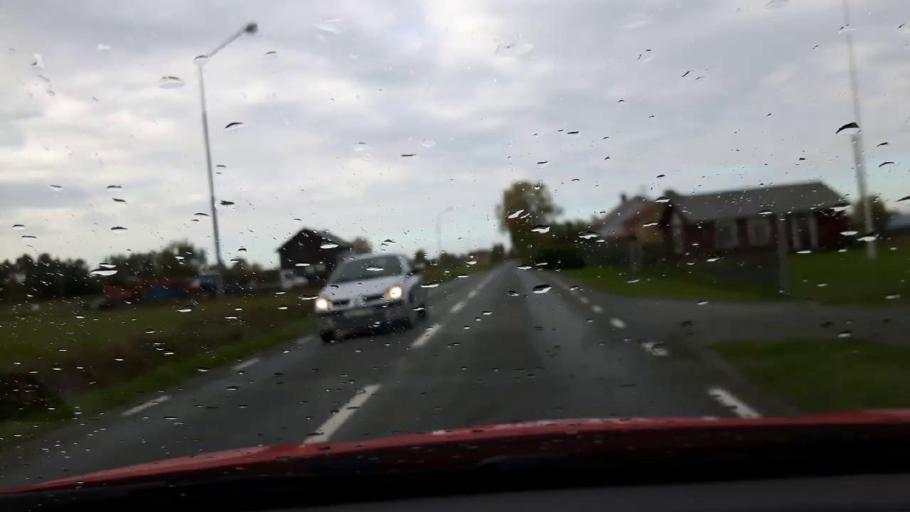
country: SE
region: Jaemtland
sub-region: Krokoms Kommun
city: Krokom
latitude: 63.1296
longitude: 14.2861
